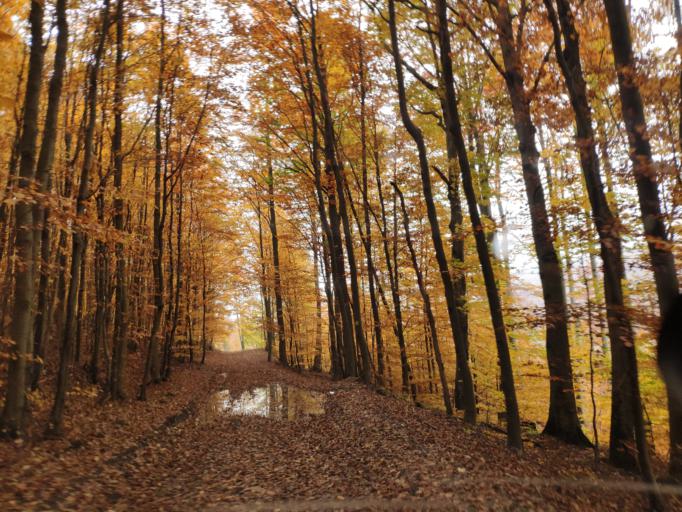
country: SK
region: Kosicky
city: Moldava nad Bodvou
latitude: 48.7347
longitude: 21.0254
